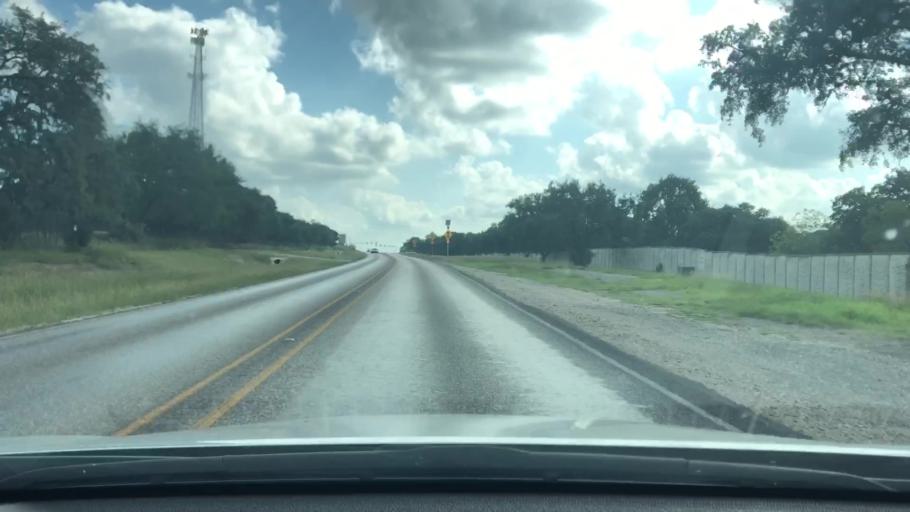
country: US
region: Texas
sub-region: Bexar County
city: Fair Oaks Ranch
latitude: 29.7353
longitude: -98.6235
